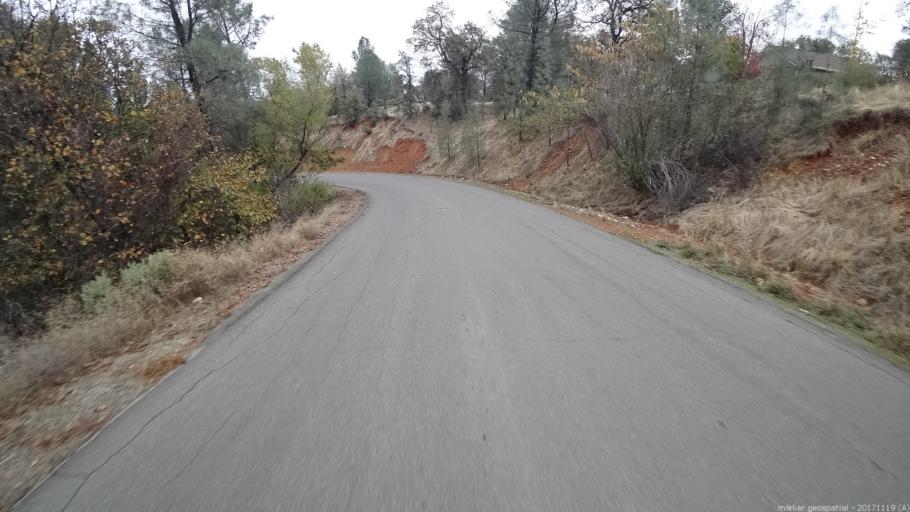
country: US
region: California
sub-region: Shasta County
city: Redding
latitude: 40.4907
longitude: -122.4101
